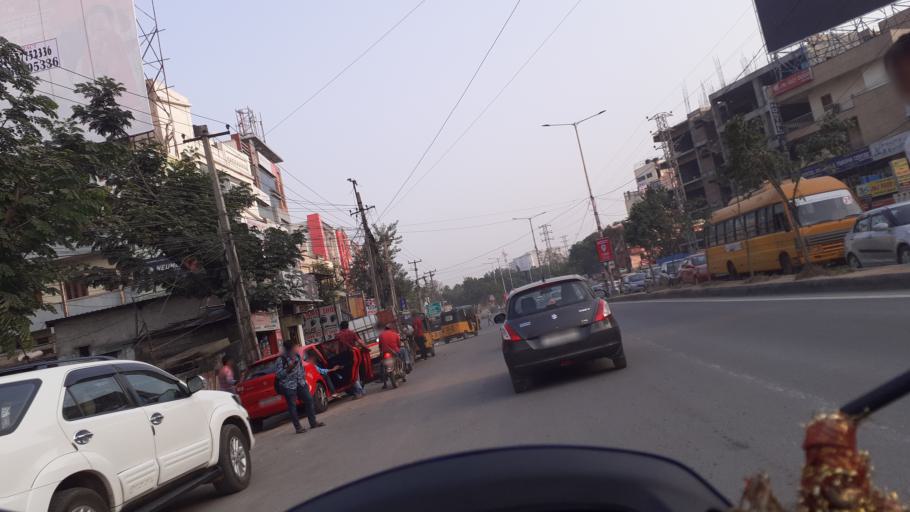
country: IN
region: Telangana
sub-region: Medak
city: Serilingampalle
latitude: 17.4934
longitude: 78.3517
